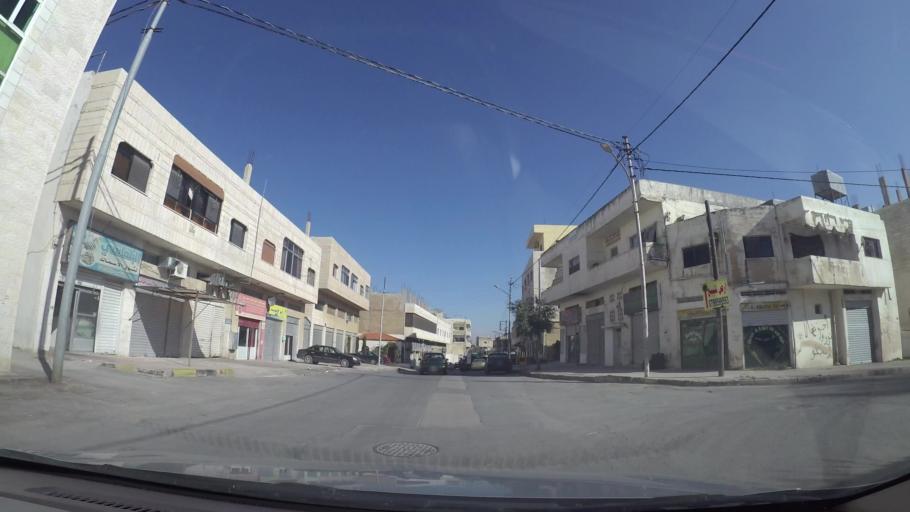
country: JO
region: Amman
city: Al Bunayyat ash Shamaliyah
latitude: 31.9069
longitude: 35.9067
